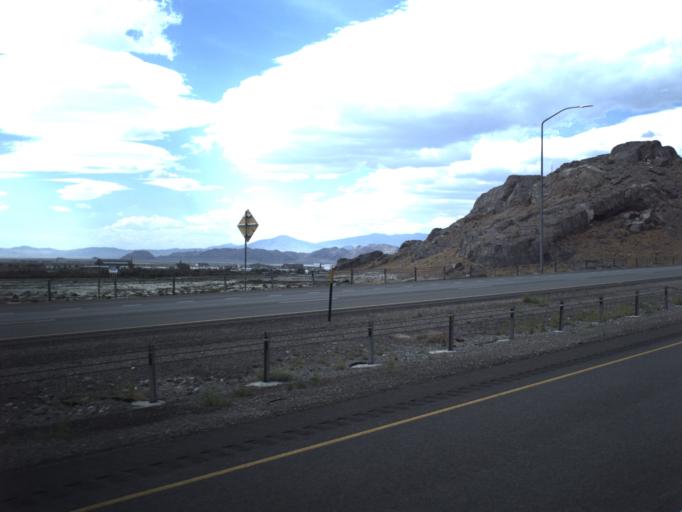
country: US
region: Utah
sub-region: Tooele County
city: Wendover
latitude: 40.7444
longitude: -114.0237
